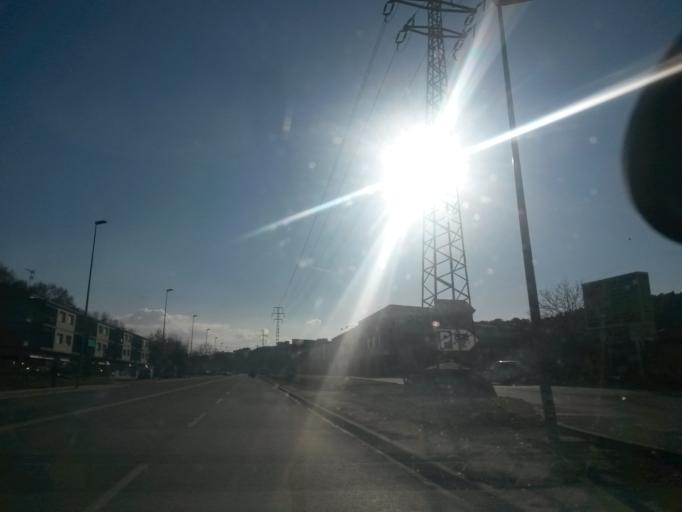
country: ES
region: Catalonia
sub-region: Provincia de Girona
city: Sarria de Ter
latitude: 42.0066
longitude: 2.8165
